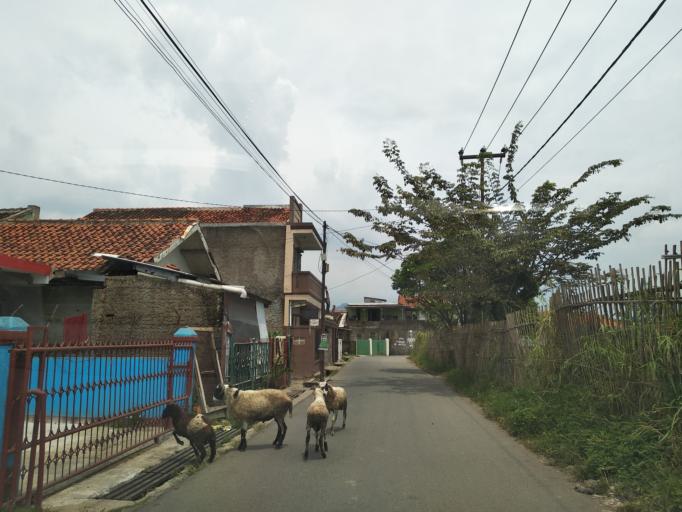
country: ID
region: West Java
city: Pameungpeuk
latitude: -6.9734
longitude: 107.6478
